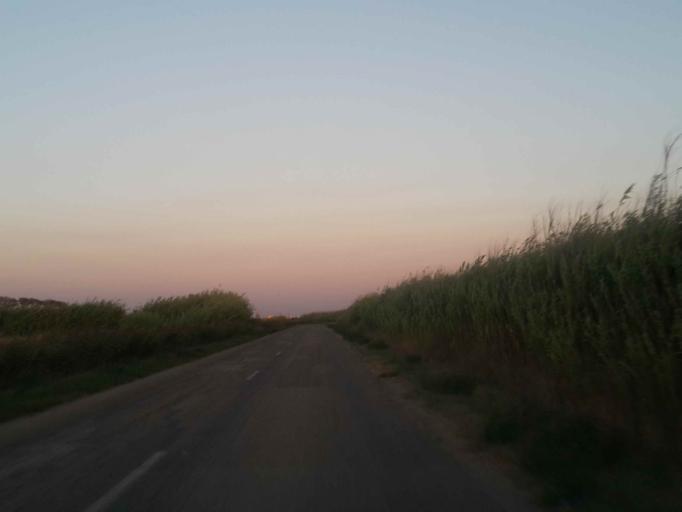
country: FR
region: Provence-Alpes-Cote d'Azur
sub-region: Departement des Bouches-du-Rhone
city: Port-Saint-Louis-du-Rhone
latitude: 43.4285
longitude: 4.6991
